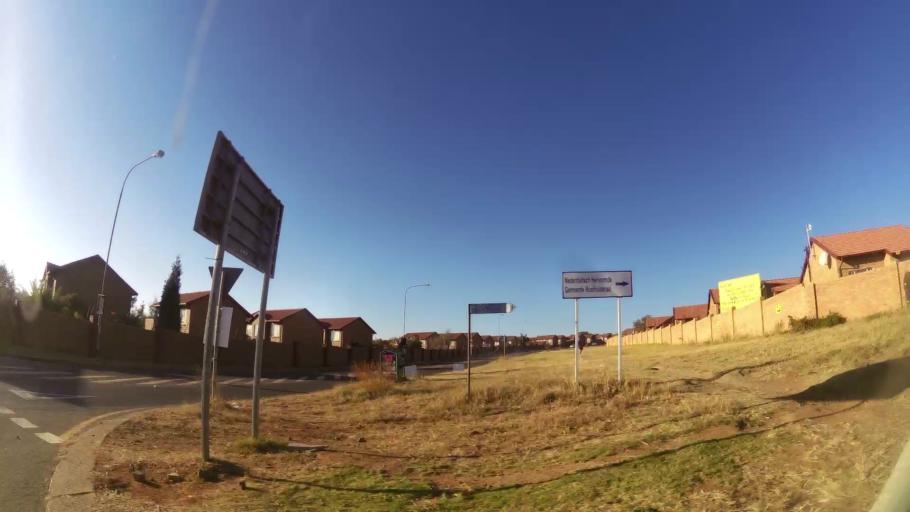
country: ZA
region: Gauteng
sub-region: City of Tshwane Metropolitan Municipality
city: Centurion
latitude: -25.9021
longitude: 28.1442
